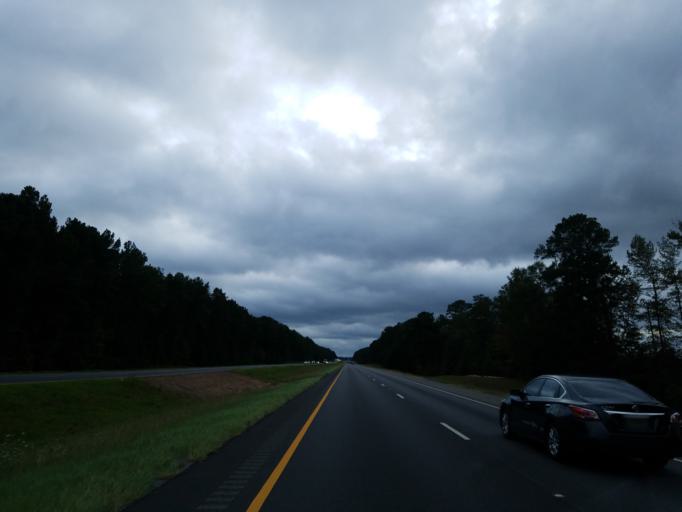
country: US
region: Alabama
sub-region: Hale County
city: Moundville
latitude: 33.0334
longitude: -87.7384
